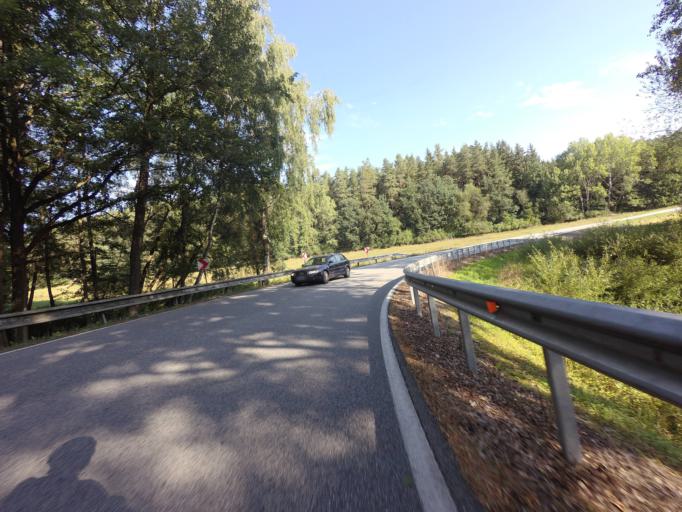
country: CZ
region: Jihocesky
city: Tyn nad Vltavou
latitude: 49.2628
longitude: 14.4109
